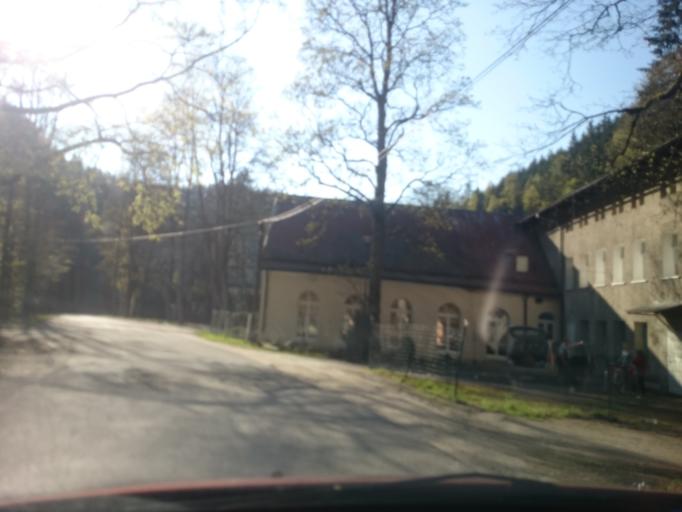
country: PL
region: Lower Silesian Voivodeship
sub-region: Powiat klodzki
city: Duszniki-Zdroj
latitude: 50.3795
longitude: 16.3948
